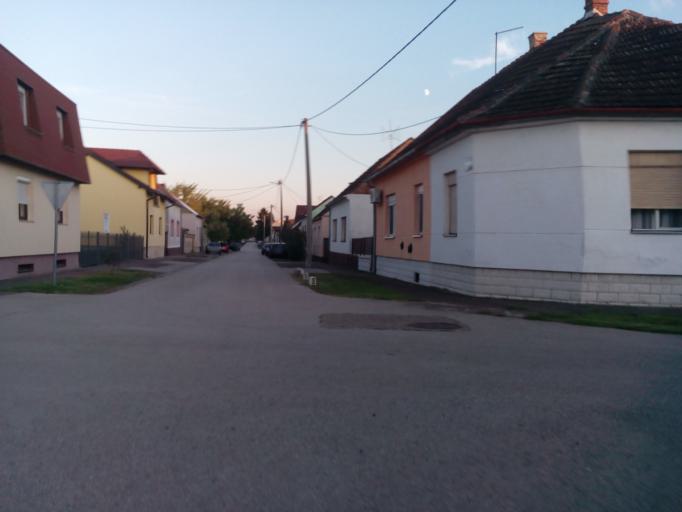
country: HR
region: Vukovarsko-Srijemska
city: Vinkovci
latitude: 45.3002
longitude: 18.8134
